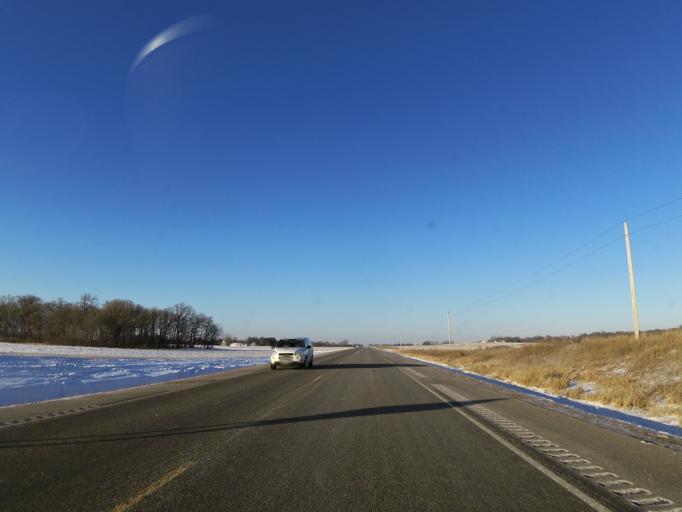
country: US
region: Minnesota
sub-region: Rice County
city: Lonsdale
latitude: 44.4914
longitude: -93.4427
